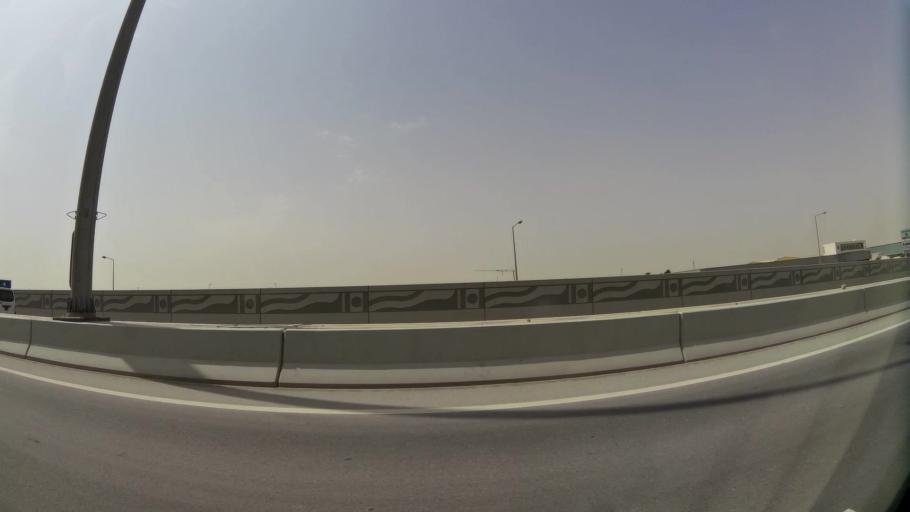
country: QA
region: Baladiyat ar Rayyan
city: Ar Rayyan
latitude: 25.2051
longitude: 51.4465
